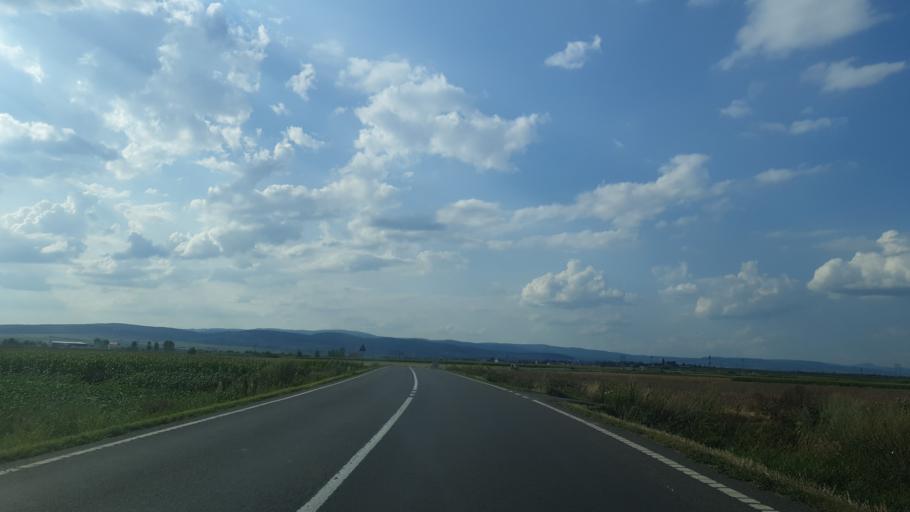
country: RO
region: Covasna
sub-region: Comuna Chichis
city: Chichis
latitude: 45.7924
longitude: 25.8060
